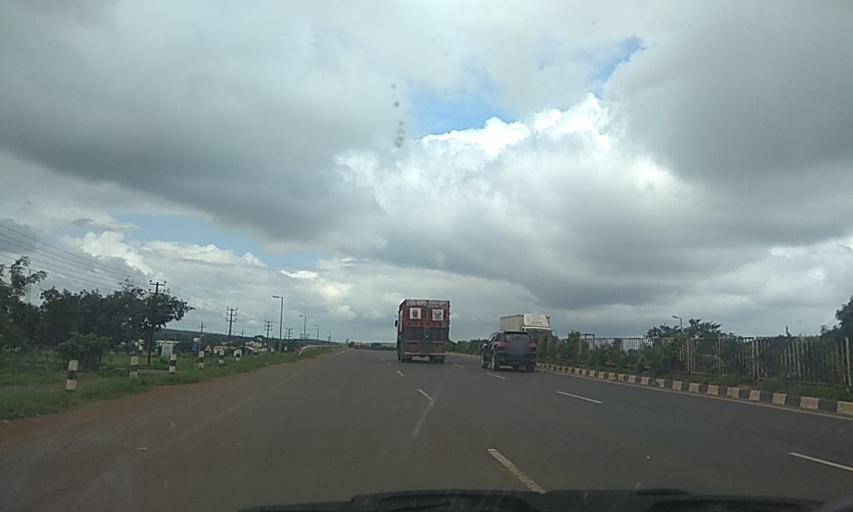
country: IN
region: Karnataka
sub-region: Dharwad
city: Alnavar
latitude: 15.5165
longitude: 74.9270
